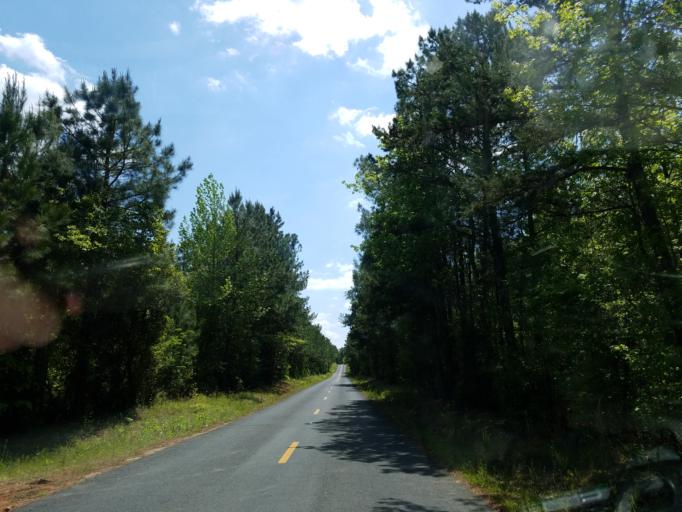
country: US
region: Georgia
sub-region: Butts County
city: Indian Springs
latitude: 33.1503
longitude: -84.0050
